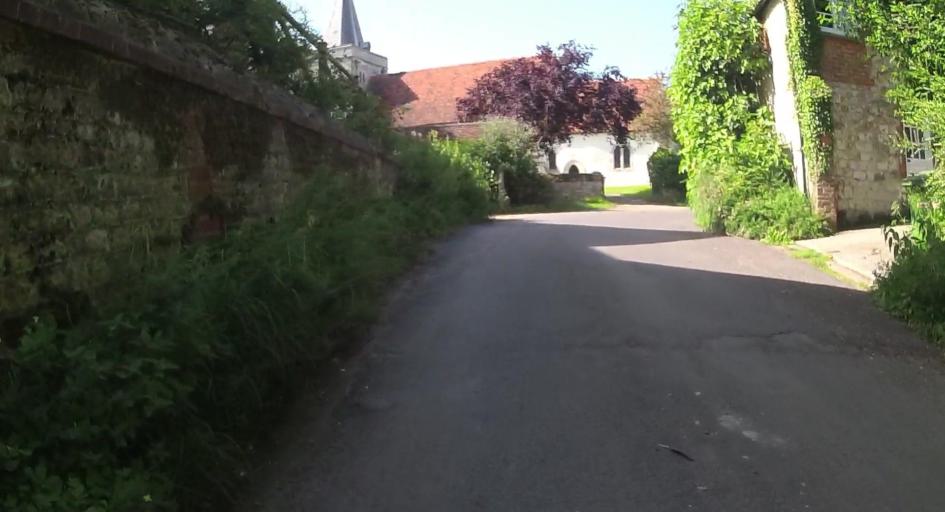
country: GB
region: England
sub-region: Hampshire
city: Kingsley
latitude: 51.1621
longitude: -0.8978
